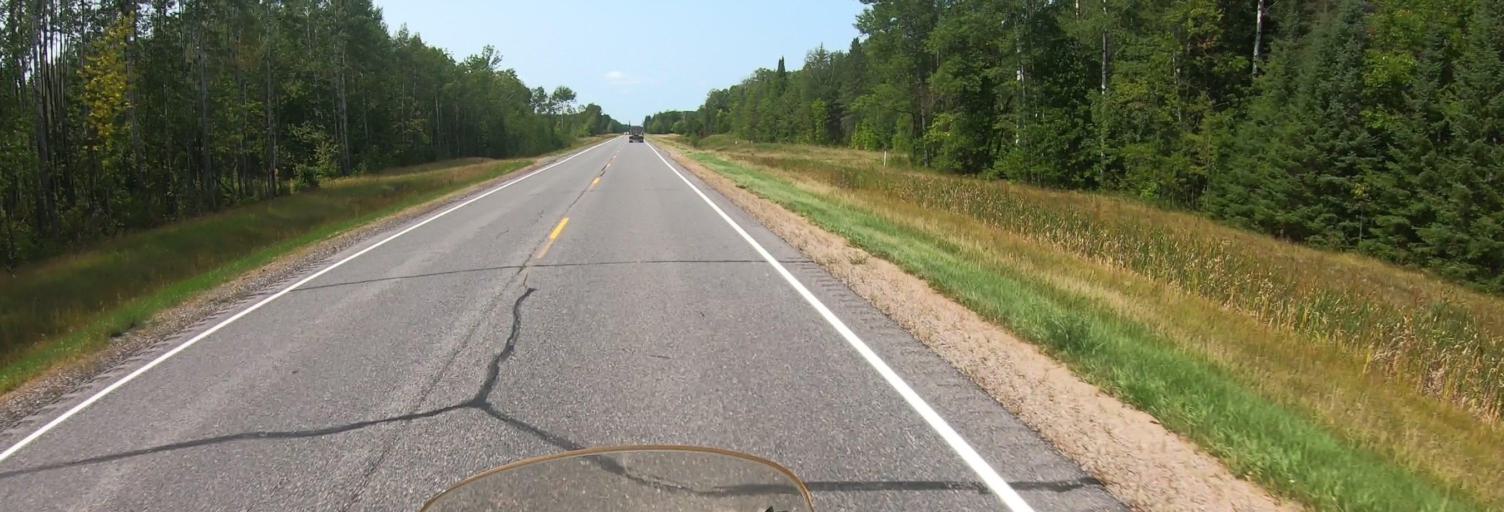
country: US
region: Minnesota
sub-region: Koochiching County
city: International Falls
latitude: 48.5127
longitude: -93.7656
